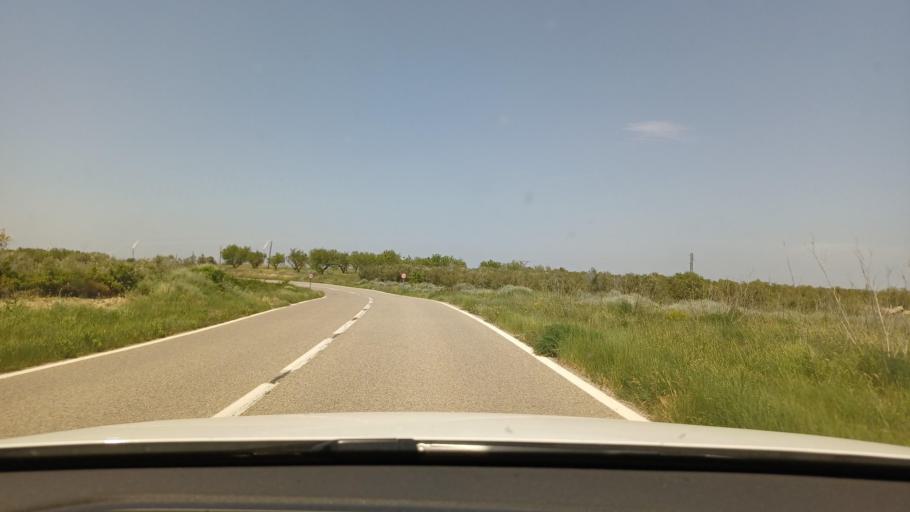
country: ES
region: Catalonia
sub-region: Provincia de Tarragona
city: Vilalba dels Arcs
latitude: 41.1105
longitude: 0.4172
